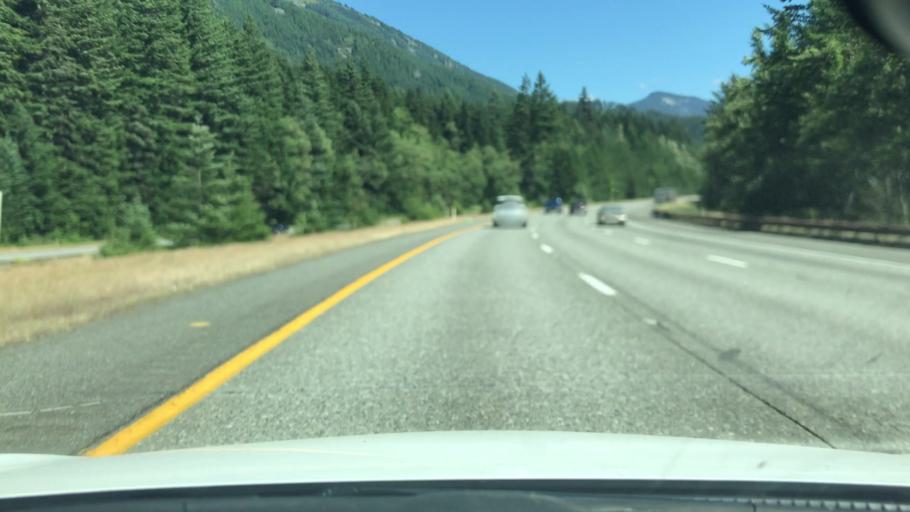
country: US
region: Washington
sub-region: King County
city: Tanner
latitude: 47.4245
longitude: -121.5978
